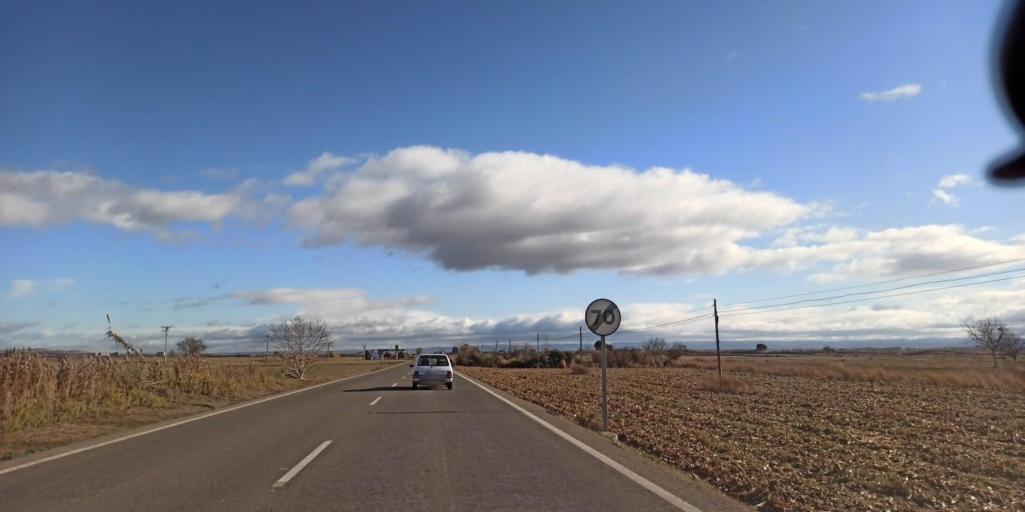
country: ES
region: Catalonia
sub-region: Provincia de Lleida
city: Bellcaire d'Urgell
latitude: 41.7562
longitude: 0.9101
